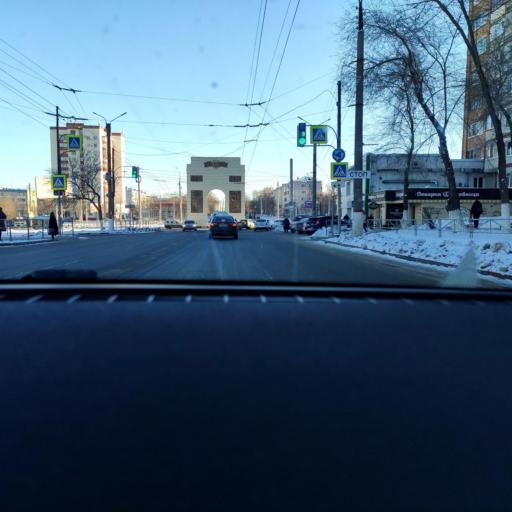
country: RU
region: Samara
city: Novokuybyshevsk
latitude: 53.0967
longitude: 49.9693
